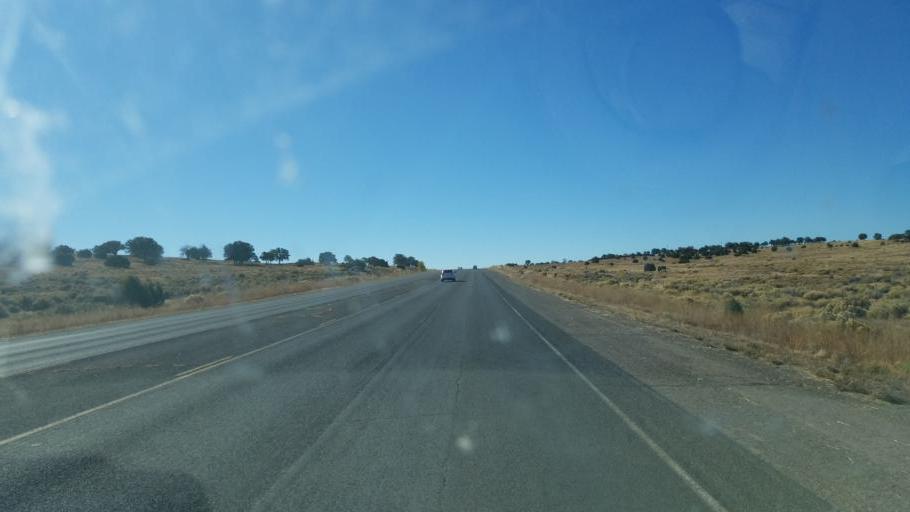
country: US
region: Arizona
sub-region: Apache County
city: Window Rock
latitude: 35.7045
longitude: -109.0633
